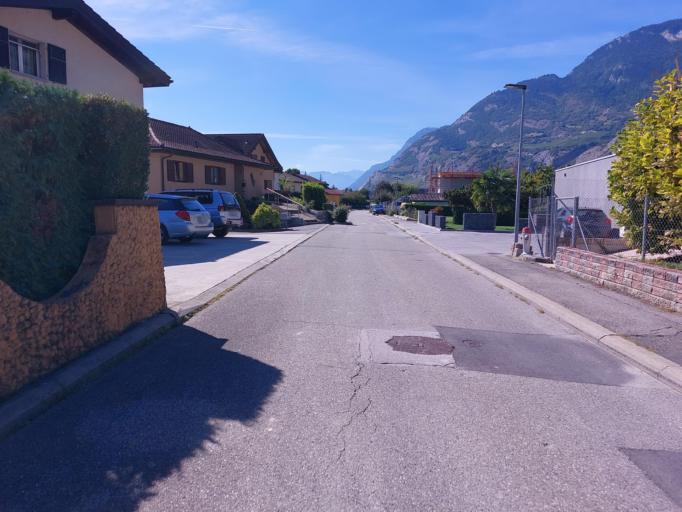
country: CH
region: Valais
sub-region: Conthey District
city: Vetroz
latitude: 46.2214
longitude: 7.2815
